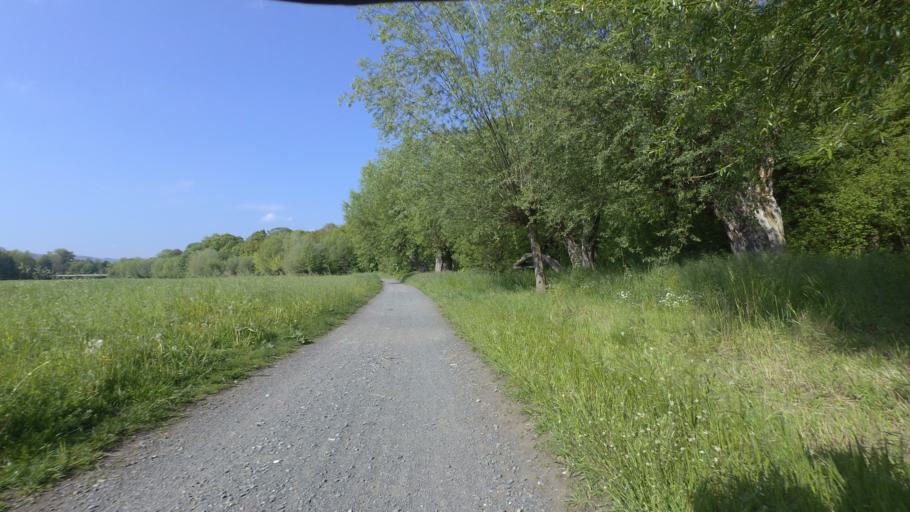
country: DE
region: Saxony-Anhalt
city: Wernigerode
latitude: 51.8600
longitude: 10.8097
